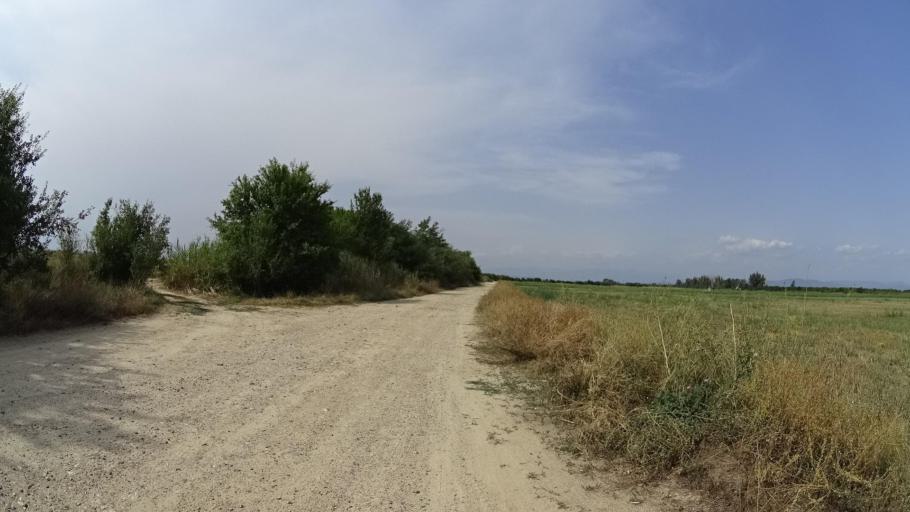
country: BG
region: Plovdiv
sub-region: Obshtina Kaloyanovo
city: Kaloyanovo
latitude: 42.2915
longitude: 24.7962
